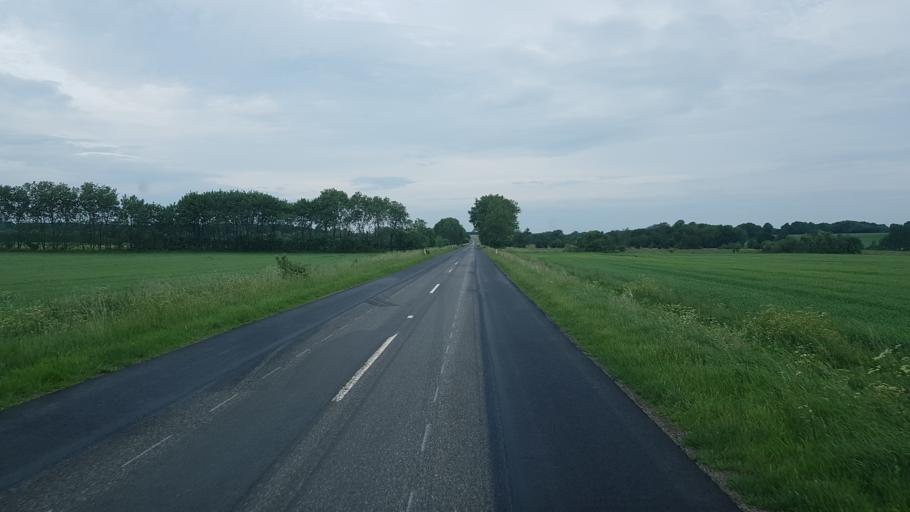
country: DK
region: South Denmark
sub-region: Vejen Kommune
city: Brorup
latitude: 55.4399
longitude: 8.9669
